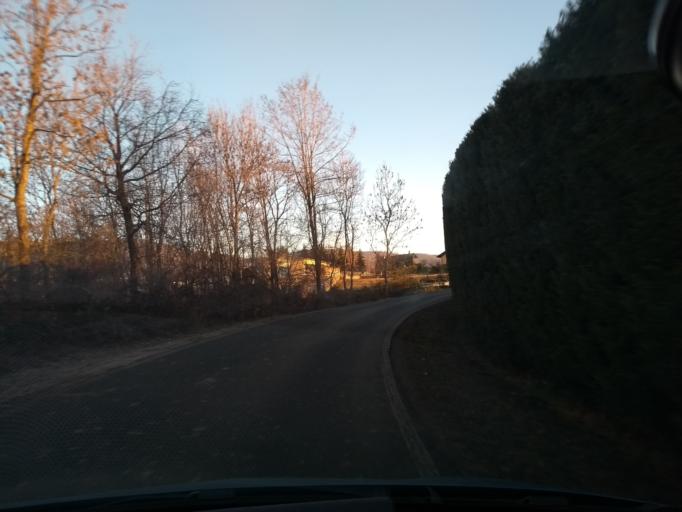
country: IT
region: Piedmont
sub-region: Provincia di Torino
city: Mathi
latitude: 45.2844
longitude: 7.5450
